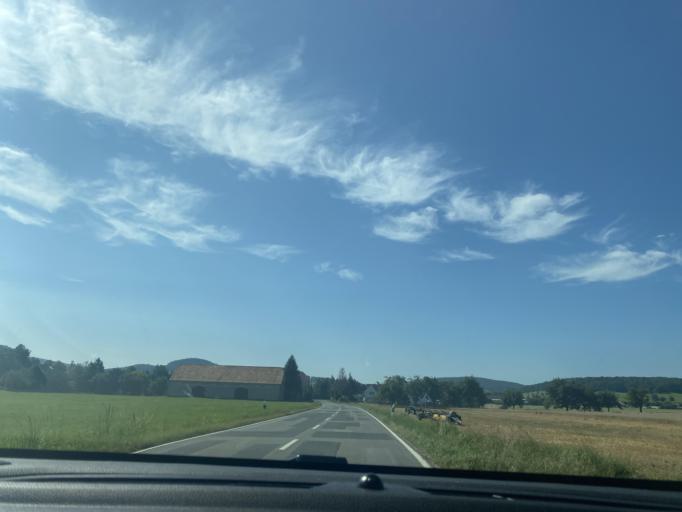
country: DE
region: Saxony
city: Grosshennersdorf
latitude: 51.0006
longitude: 14.7947
